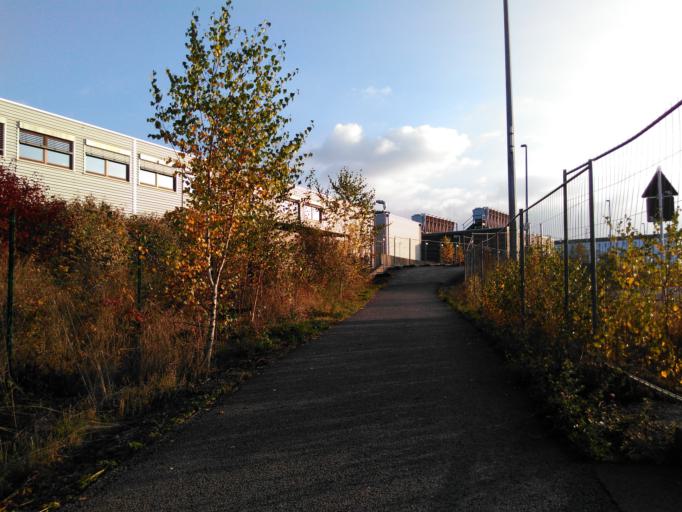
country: LU
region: Luxembourg
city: Belvaux
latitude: 49.5062
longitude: 5.9430
